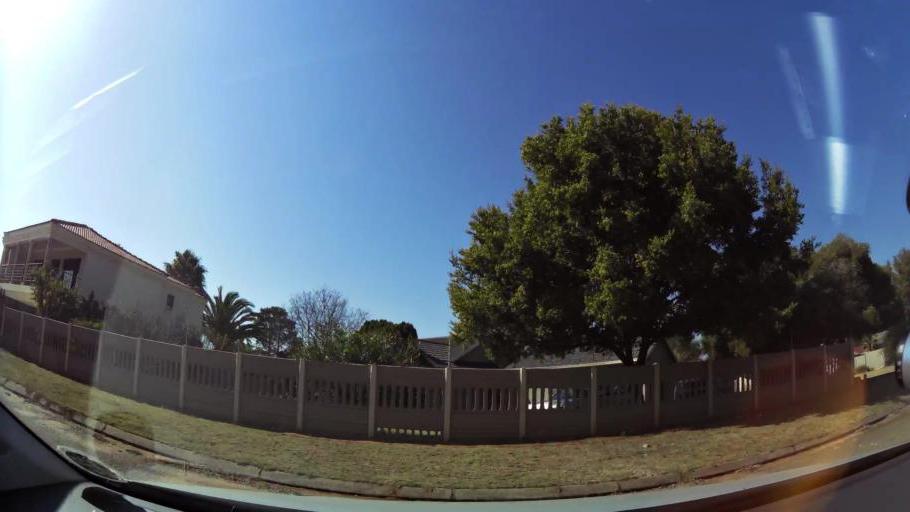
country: ZA
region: Gauteng
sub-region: Ekurhuleni Metropolitan Municipality
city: Tembisa
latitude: -26.0482
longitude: 28.2074
